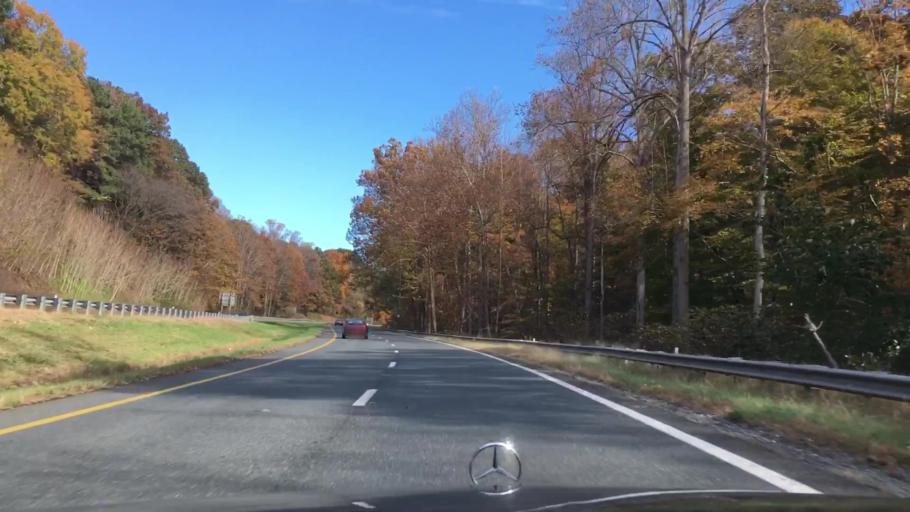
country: US
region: Virginia
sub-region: Campbell County
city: Altavista
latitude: 37.1416
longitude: -79.2400
